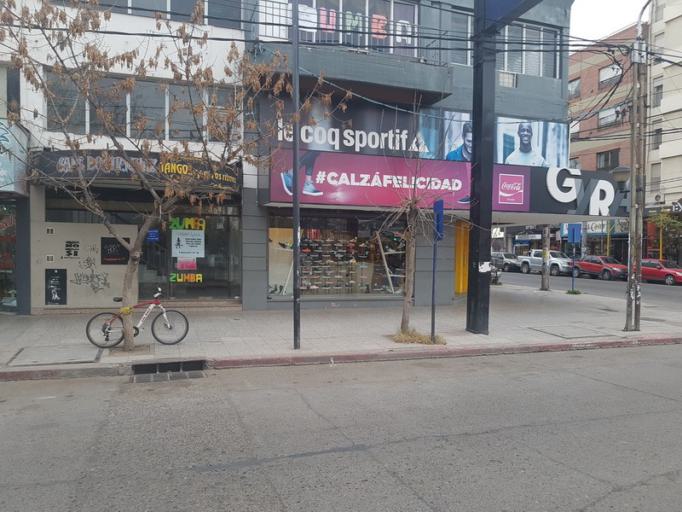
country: AR
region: Neuquen
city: Neuquen
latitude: -38.9583
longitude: -68.0595
